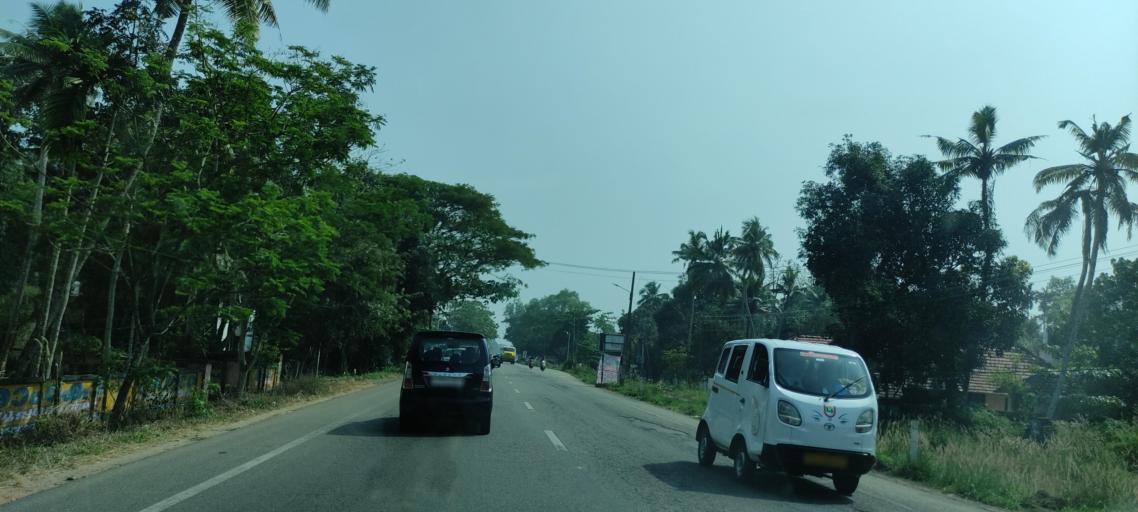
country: IN
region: Kerala
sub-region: Alappuzha
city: Kayankulam
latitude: 9.2403
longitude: 76.4702
